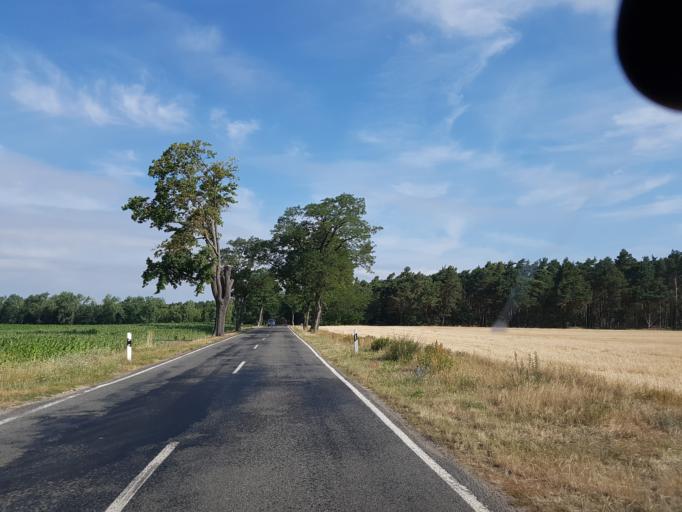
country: DE
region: Brandenburg
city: Ihlow
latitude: 51.9823
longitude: 13.2984
